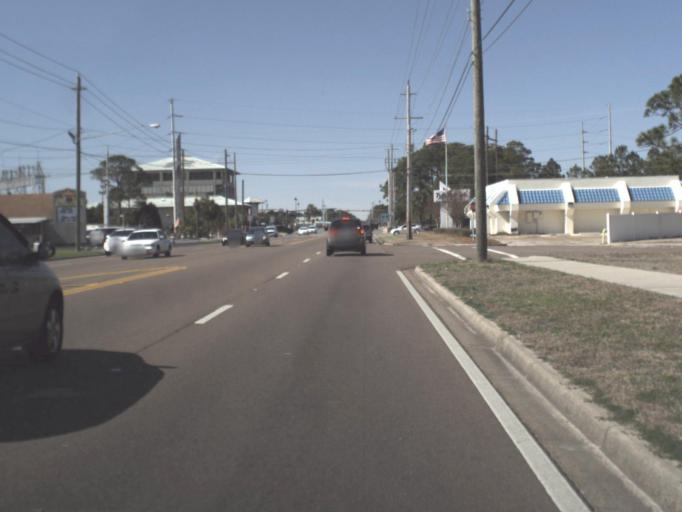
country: US
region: Florida
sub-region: Bay County
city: Panama City Beach
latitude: 30.1868
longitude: -85.8137
